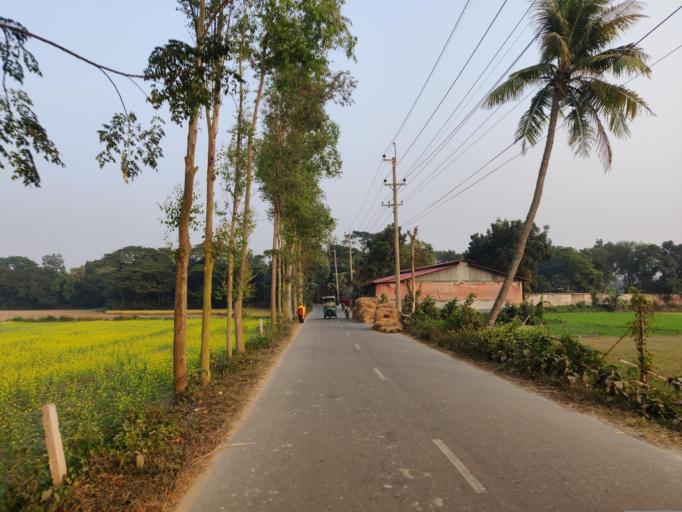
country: BD
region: Dhaka
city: Bajitpur
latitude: 24.1584
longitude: 90.7589
